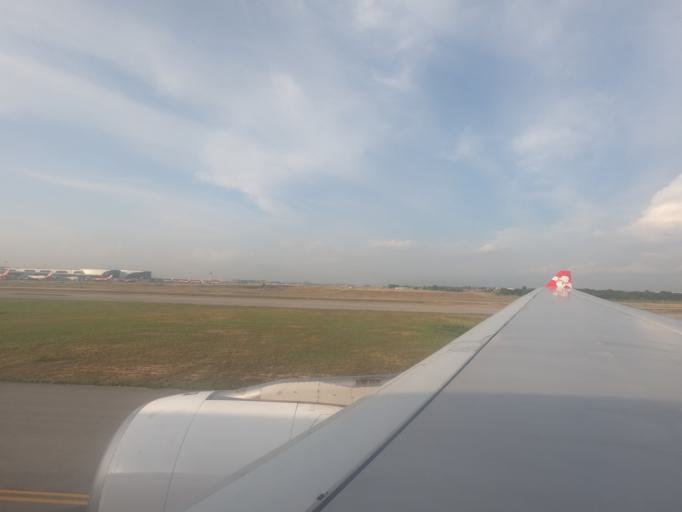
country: MY
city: Sungai Pelek New Village
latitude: 2.7301
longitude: 101.6850
